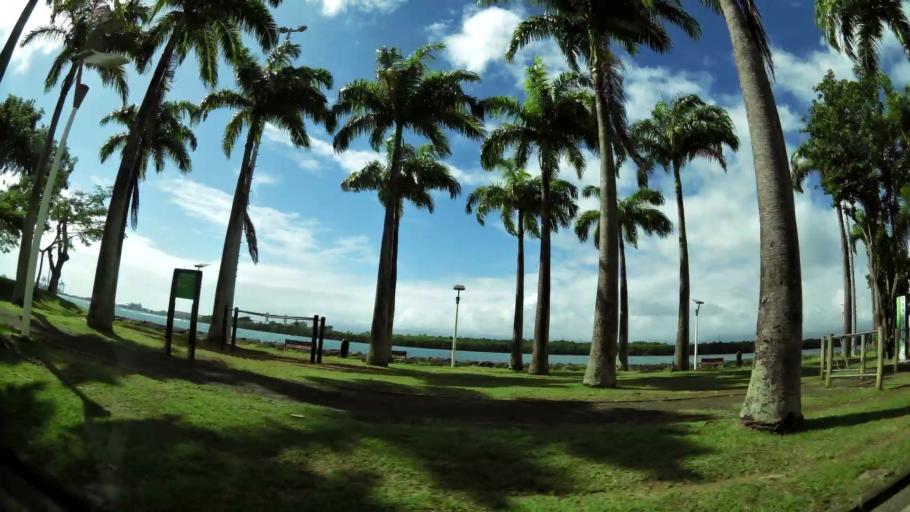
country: GP
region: Guadeloupe
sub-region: Guadeloupe
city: Pointe-a-Pitre
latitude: 16.2492
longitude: -61.5471
